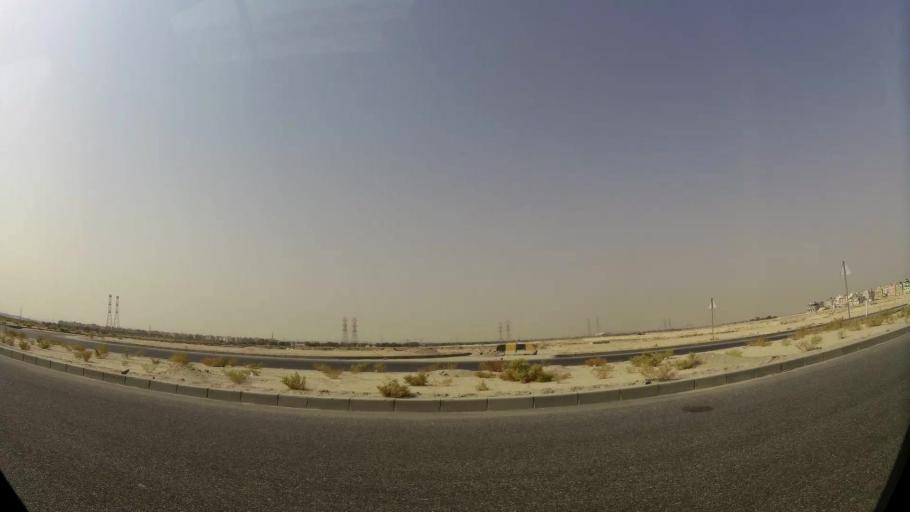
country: KW
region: Muhafazat al Jahra'
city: Al Jahra'
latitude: 29.3380
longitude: 47.7497
